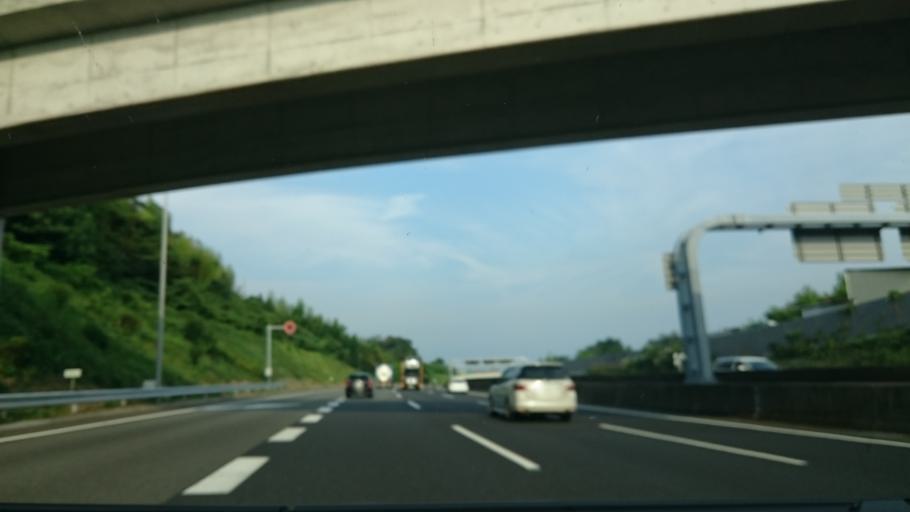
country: JP
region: Mie
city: Yokkaichi
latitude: 35.0361
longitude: 136.6370
